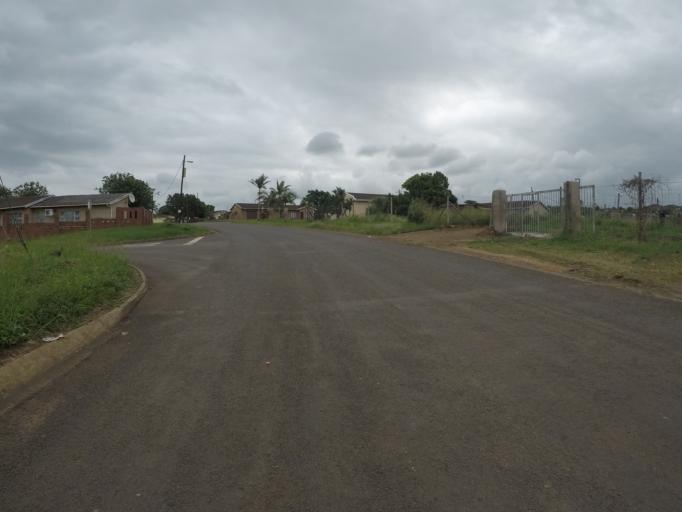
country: ZA
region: KwaZulu-Natal
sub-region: uThungulu District Municipality
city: Empangeni
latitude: -28.7783
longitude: 31.8573
